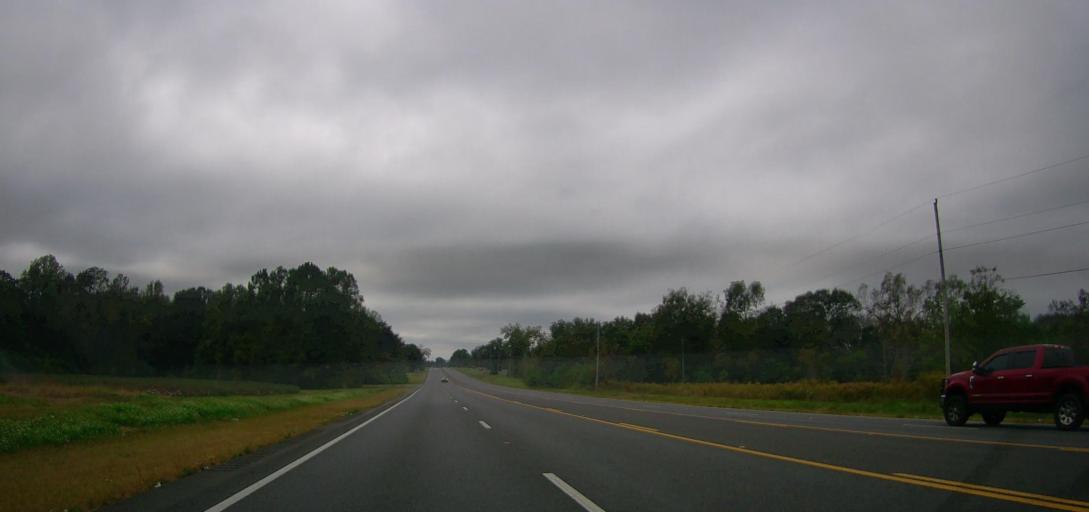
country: US
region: Georgia
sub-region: Thomas County
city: Thomasville
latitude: 30.9481
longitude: -83.9006
